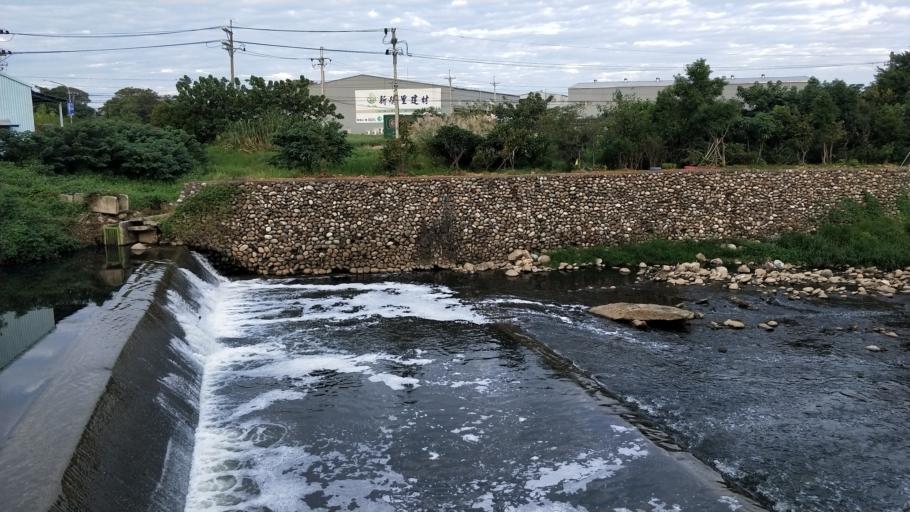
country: TW
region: Taiwan
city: Taoyuan City
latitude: 24.9794
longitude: 121.2328
